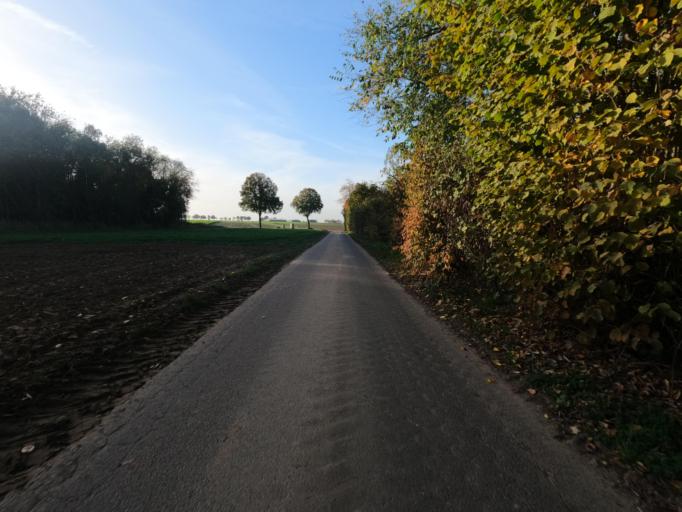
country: DE
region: North Rhine-Westphalia
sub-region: Regierungsbezirk Koln
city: Titz
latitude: 51.0483
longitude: 6.4127
